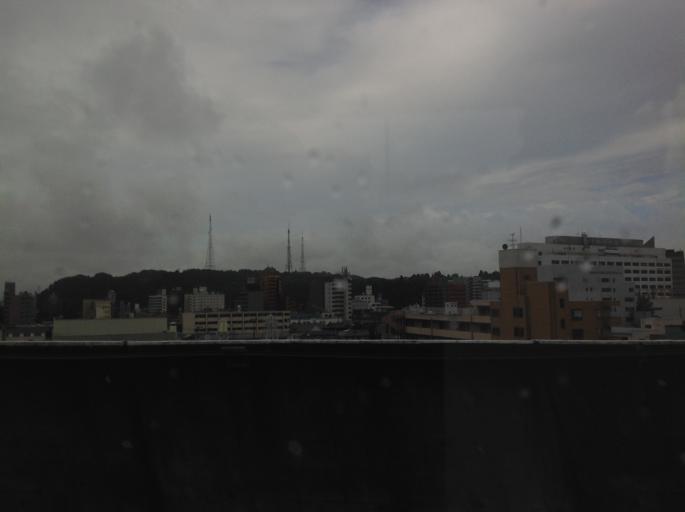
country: JP
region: Miyagi
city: Sendai
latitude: 38.2527
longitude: 140.8851
